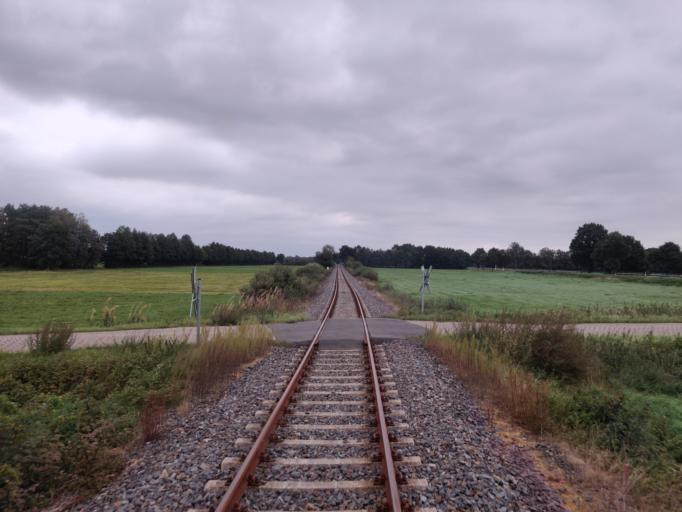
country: DE
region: Lower Saxony
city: Gnarrenburg
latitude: 53.3397
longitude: 8.9943
